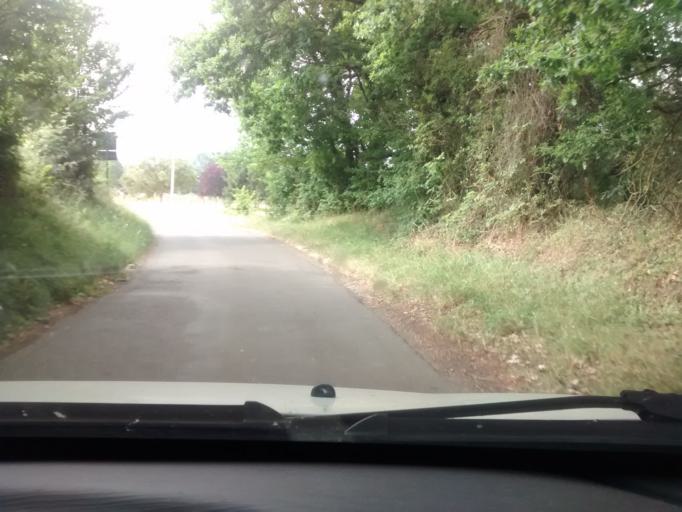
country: FR
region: Brittany
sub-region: Departement d'Ille-et-Vilaine
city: Saint-Jacques-de-la-Lande
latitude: 48.0866
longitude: -1.7292
